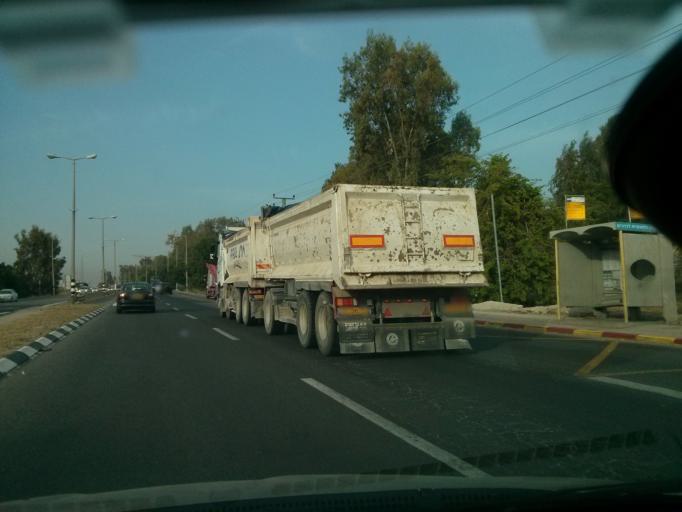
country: IL
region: Central District
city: Bene 'Ayish
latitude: 31.7274
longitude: 34.7495
